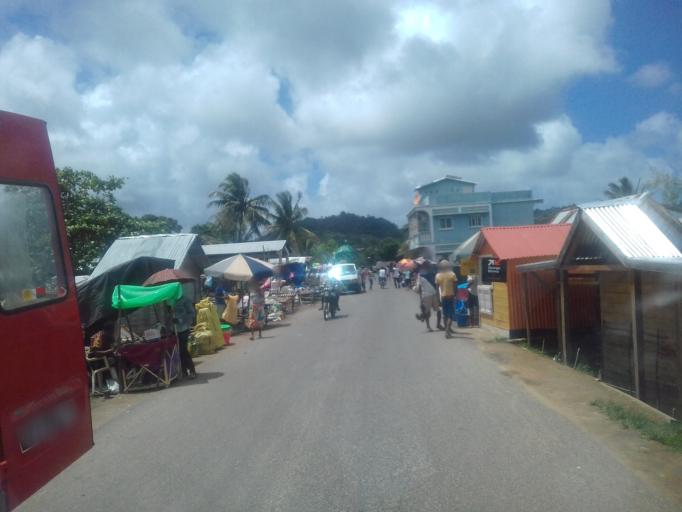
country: MG
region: Sava
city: Sambava
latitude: -14.1362
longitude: 50.0587
